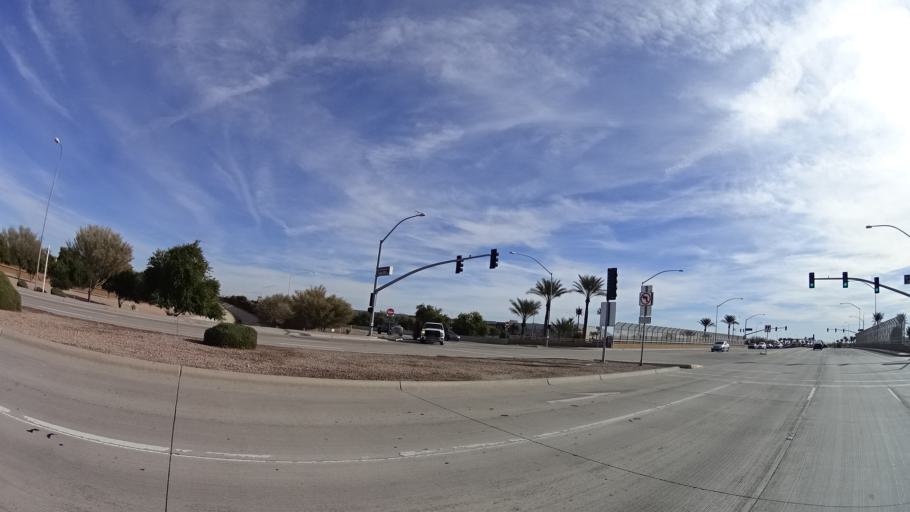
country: US
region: Arizona
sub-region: Maricopa County
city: Chandler
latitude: 33.2836
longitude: -111.8070
